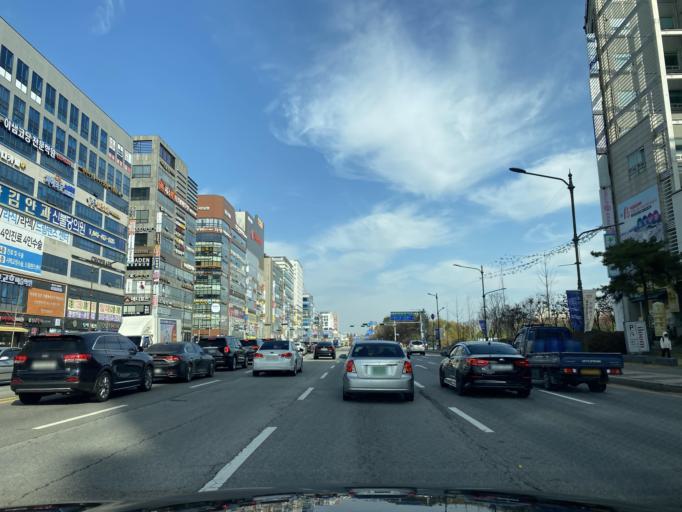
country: KR
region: Chungcheongnam-do
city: Cheonan
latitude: 36.8113
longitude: 127.1085
